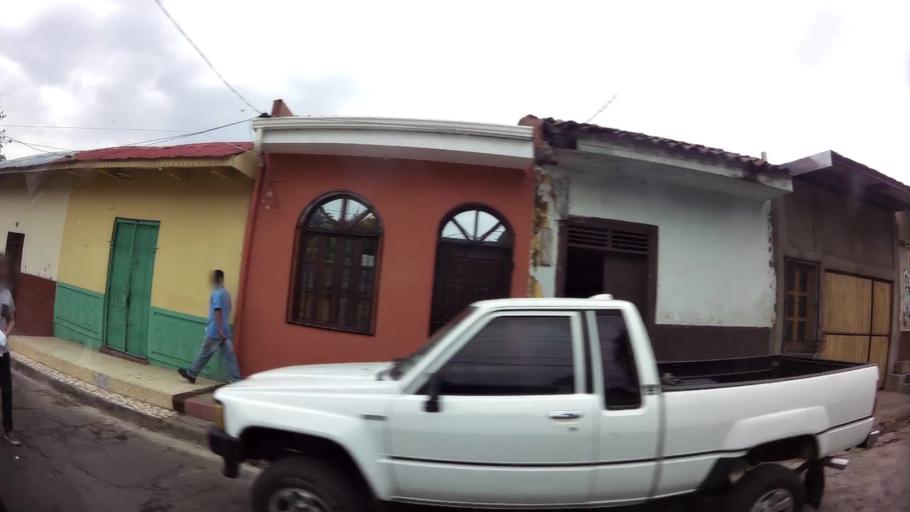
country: NI
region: Leon
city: Leon
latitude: 12.4345
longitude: -86.8732
